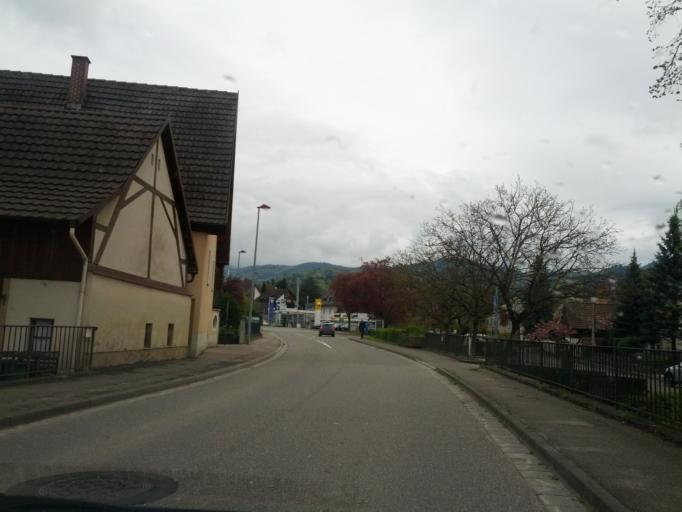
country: DE
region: Baden-Wuerttemberg
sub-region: Freiburg Region
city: Pfaffenweiler
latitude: 47.9137
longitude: 7.7552
